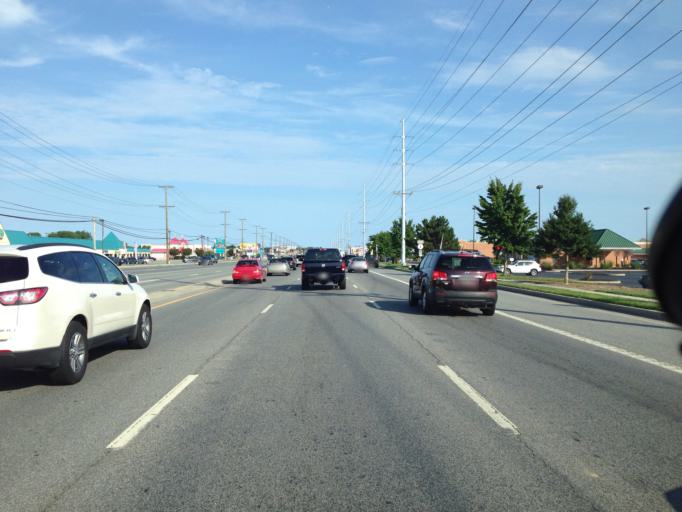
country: US
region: Delaware
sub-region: Sussex County
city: Lewes
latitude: 38.7378
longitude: -75.1430
